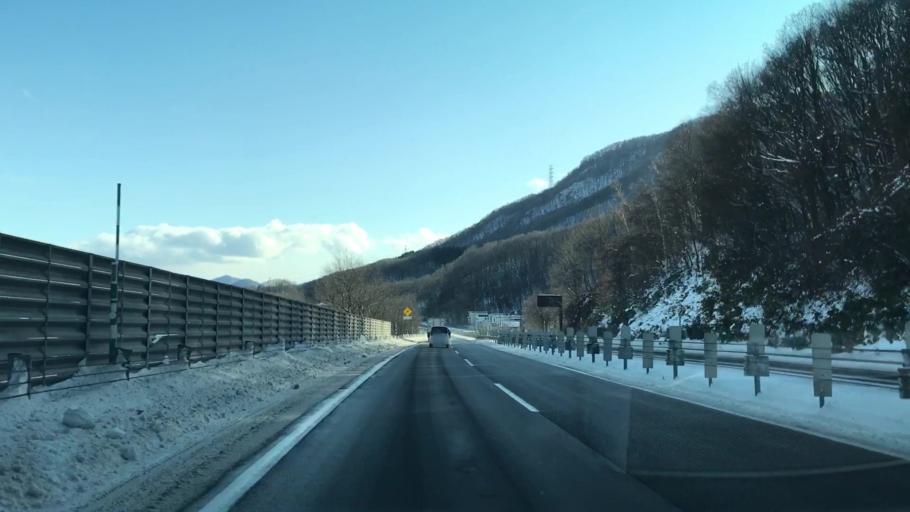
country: JP
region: Hokkaido
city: Sapporo
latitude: 43.1085
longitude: 141.2414
